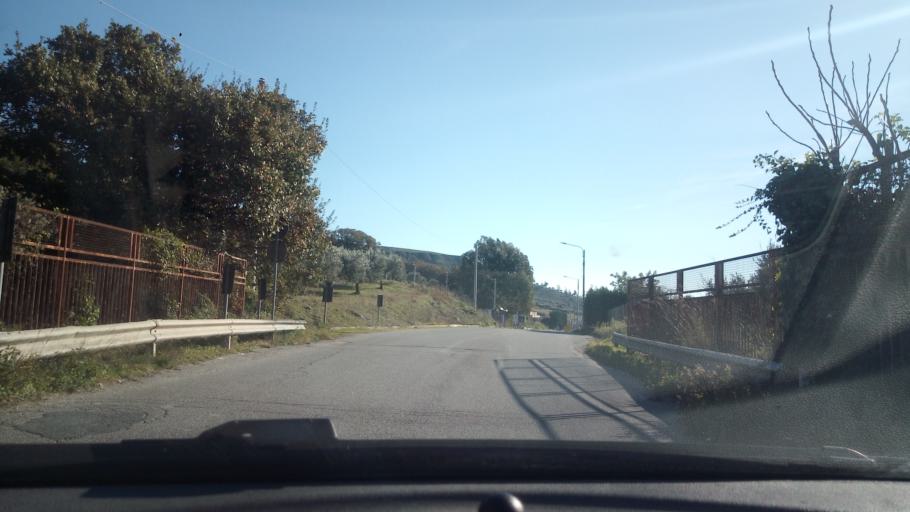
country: IT
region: Calabria
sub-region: Provincia di Catanzaro
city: Catanzaro
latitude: 38.8929
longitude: 16.5565
